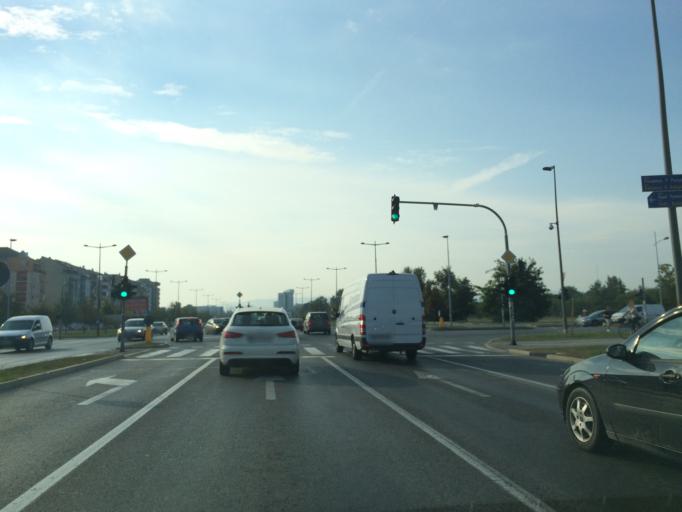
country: RS
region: Autonomna Pokrajina Vojvodina
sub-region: Juznobacki Okrug
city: Novi Sad
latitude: 45.2561
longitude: 19.8114
